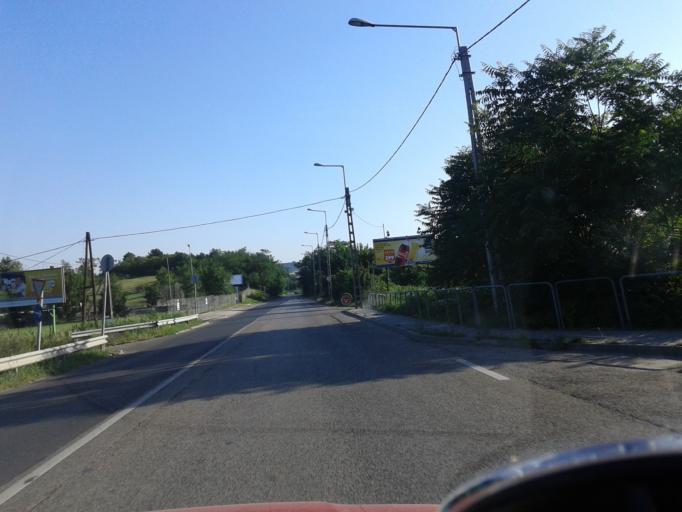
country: HU
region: Budapest
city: Budapest XI. keruelet
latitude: 47.4539
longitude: 19.0075
